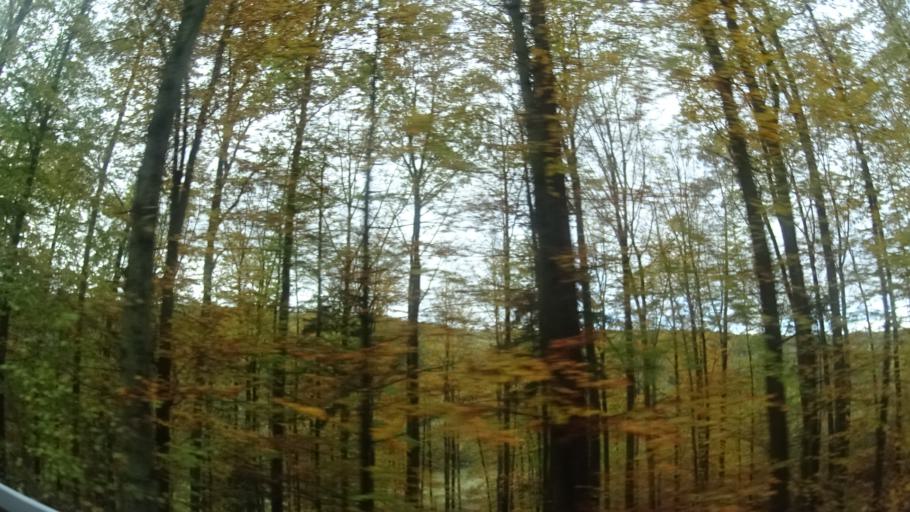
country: DE
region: Bavaria
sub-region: Regierungsbezirk Unterfranken
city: Aubstadt
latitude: 50.3518
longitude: 10.4185
